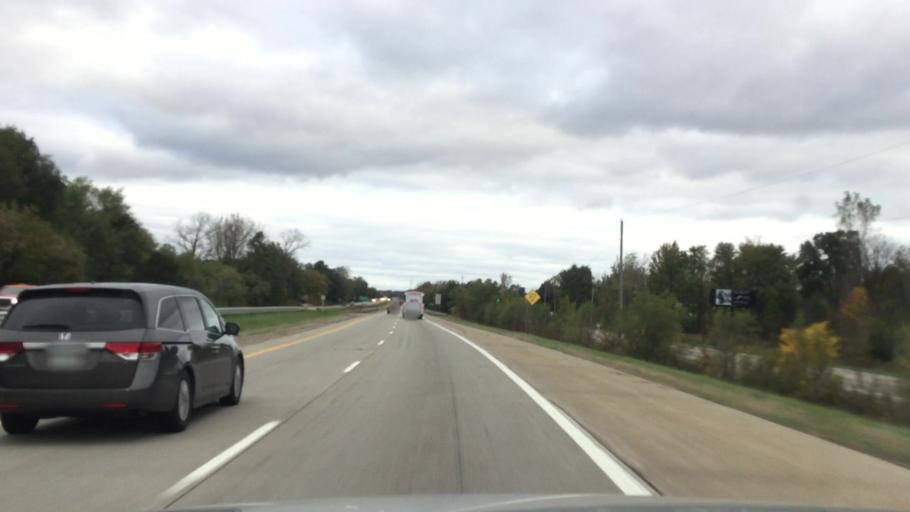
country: US
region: Michigan
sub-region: Genesee County
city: Fenton
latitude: 42.8130
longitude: -83.7251
